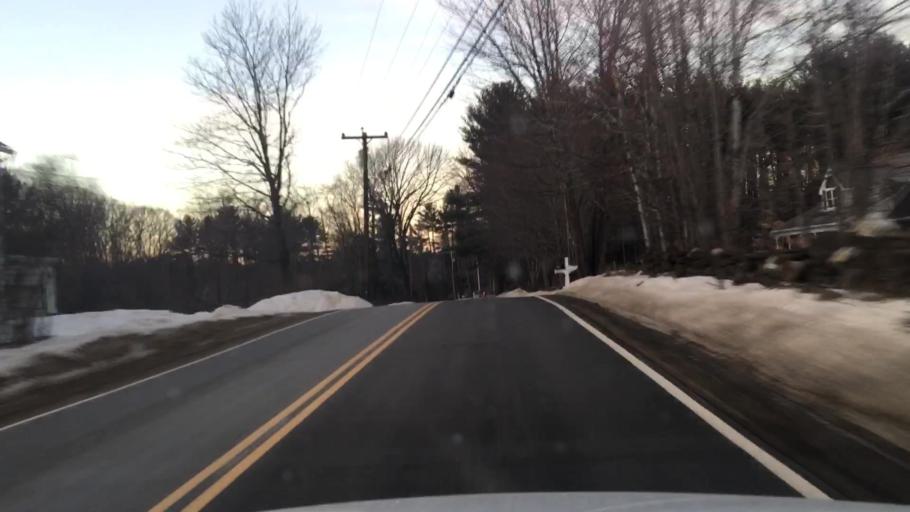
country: US
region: Maine
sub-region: York County
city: Lebanon
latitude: 43.4309
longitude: -70.8818
